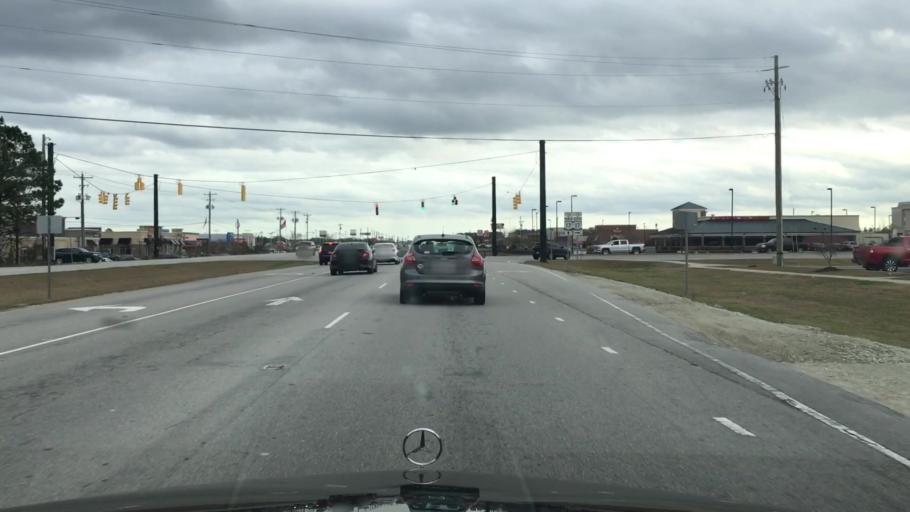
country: US
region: North Carolina
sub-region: Onslow County
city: Pumpkin Center
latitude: 34.7918
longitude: -77.4067
